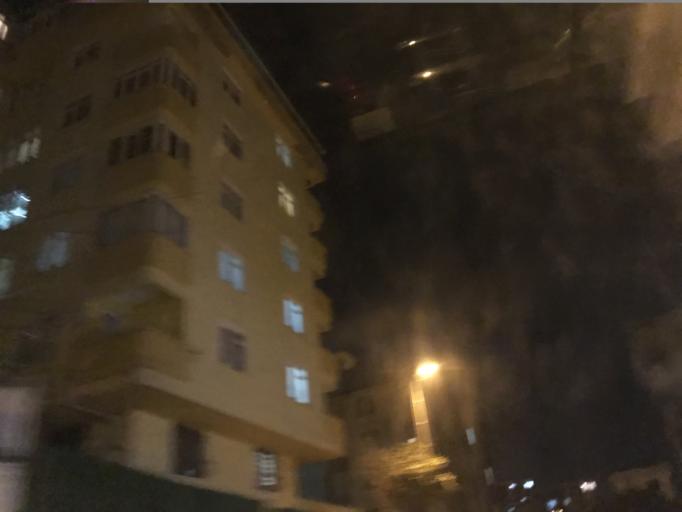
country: TR
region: Istanbul
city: Maltepe
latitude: 40.9256
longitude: 29.1451
